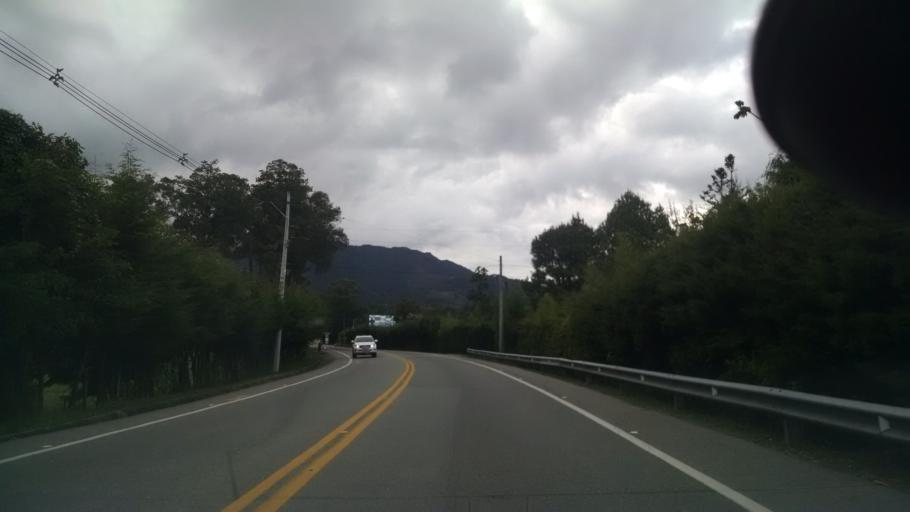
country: CO
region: Antioquia
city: El Retiro
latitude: 6.0945
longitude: -75.4989
